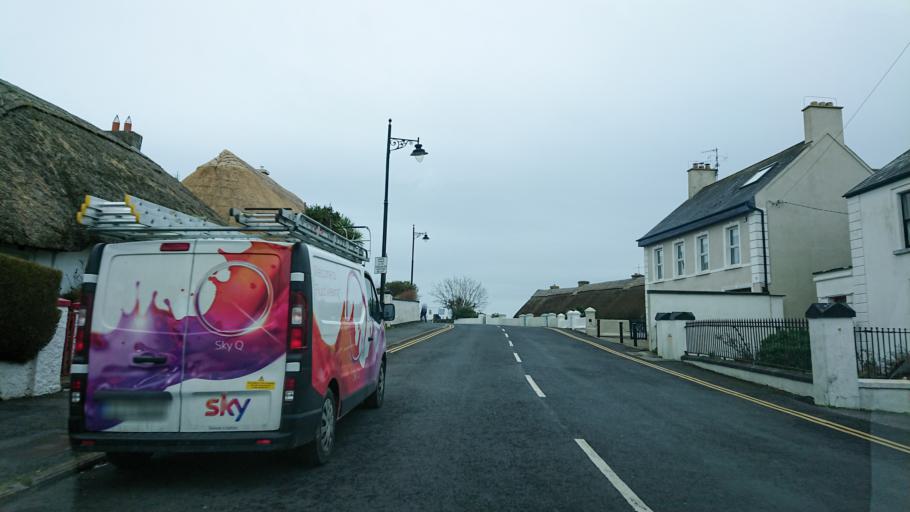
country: IE
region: Munster
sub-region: Waterford
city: Dunmore East
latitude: 52.1496
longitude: -6.9944
